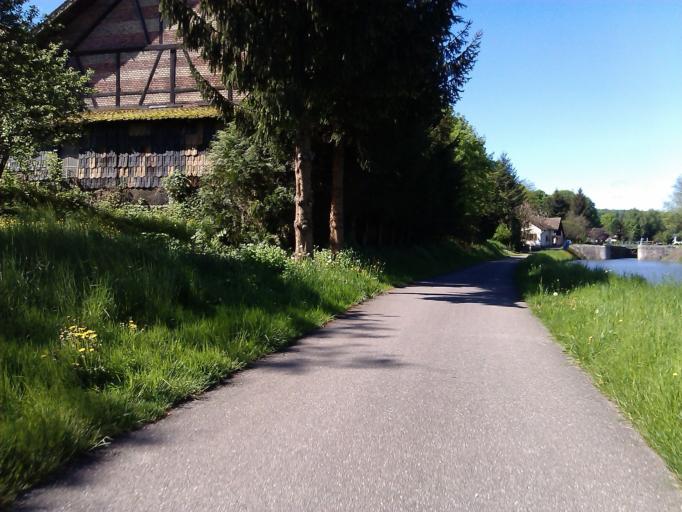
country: FR
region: Alsace
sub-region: Departement du Haut-Rhin
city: Dannemarie
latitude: 47.6331
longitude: 7.1044
